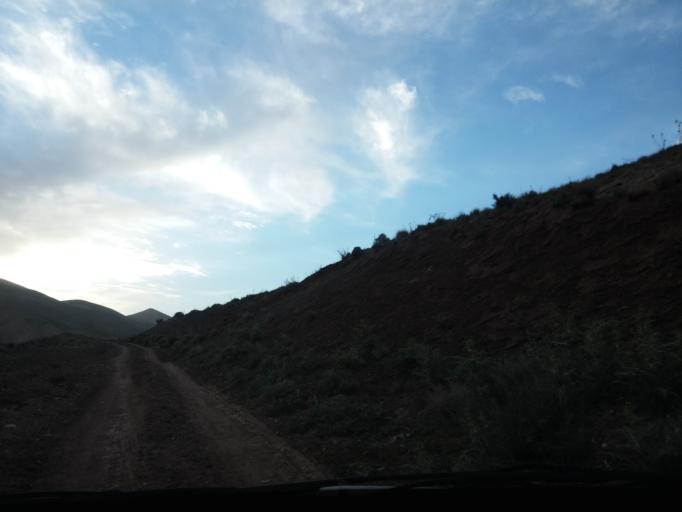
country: IR
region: Semnan
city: Istgah-e Rah Ahan-e Garmsar
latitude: 35.4737
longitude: 52.2919
